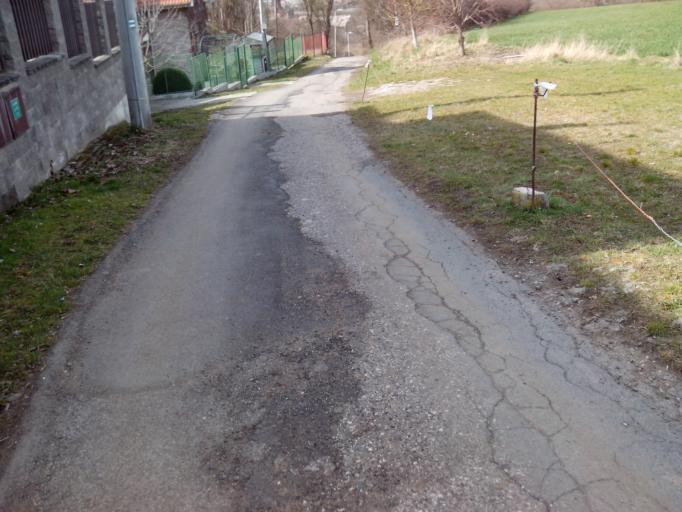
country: CZ
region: Central Bohemia
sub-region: Okres Beroun
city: Beroun
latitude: 49.9542
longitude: 14.0767
